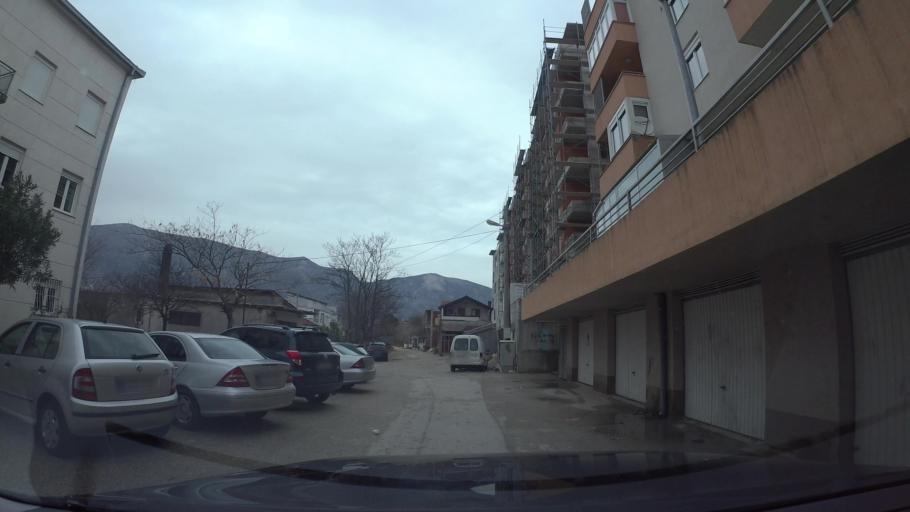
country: BA
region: Federation of Bosnia and Herzegovina
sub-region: Hercegovacko-Bosanski Kanton
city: Mostar
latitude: 43.3493
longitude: 17.8121
